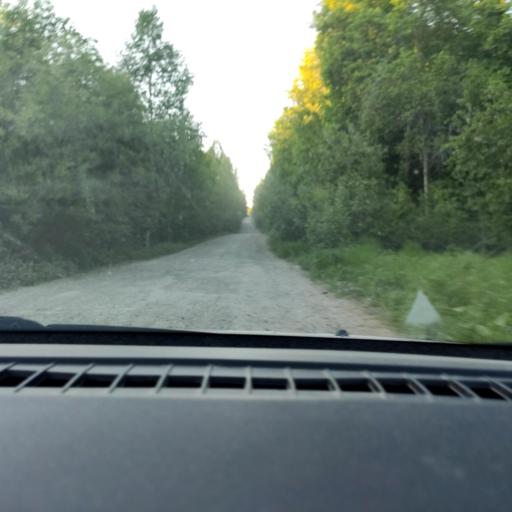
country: RU
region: Perm
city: Polazna
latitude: 58.1243
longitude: 56.4362
